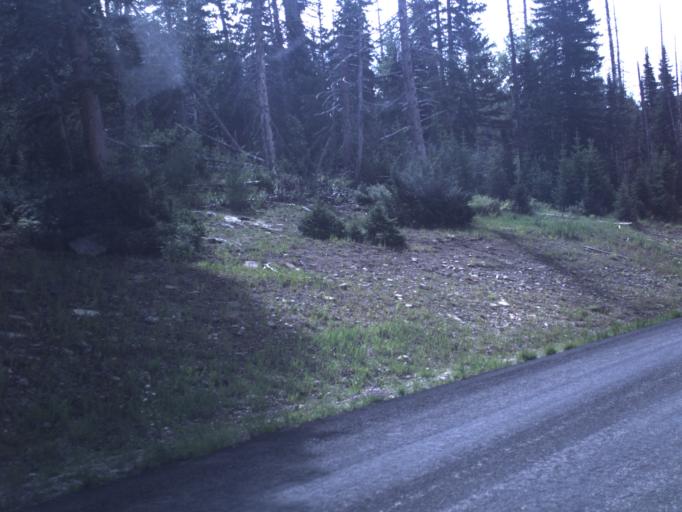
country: US
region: Utah
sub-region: Iron County
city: Cedar City
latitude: 37.5868
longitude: -112.8478
